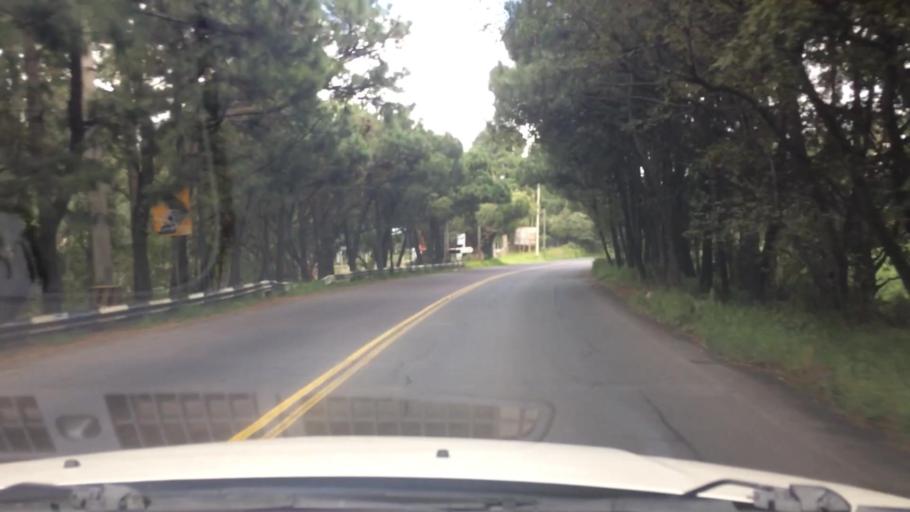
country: MX
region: Mexico City
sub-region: Tlalpan
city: Lomas de Tepemecatl
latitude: 19.2545
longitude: -99.2448
